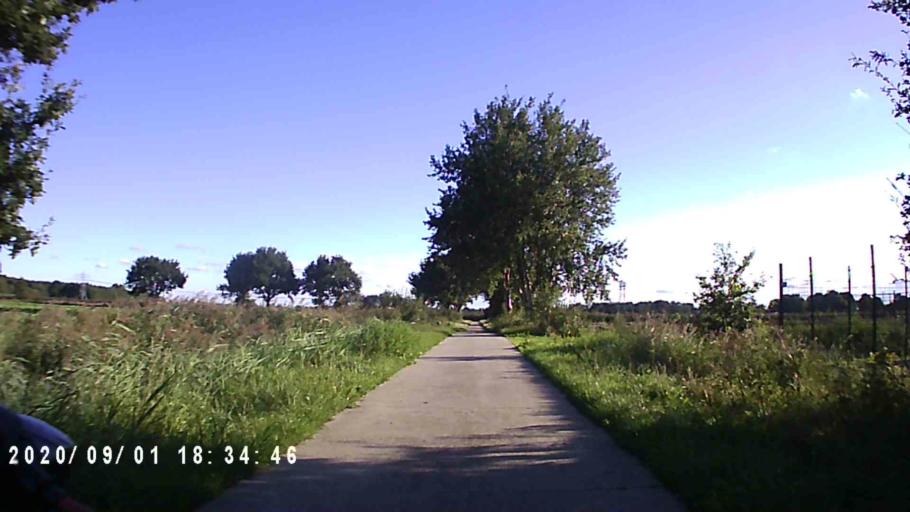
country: NL
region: Groningen
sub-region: Gemeente Hoogezand-Sappemeer
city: Sappemeer
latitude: 53.1502
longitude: 6.8030
